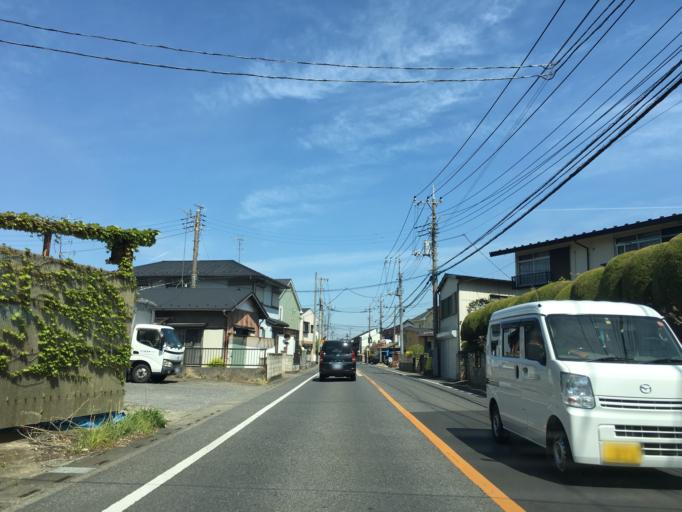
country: JP
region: Saitama
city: Sugito
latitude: 36.0200
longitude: 139.7337
